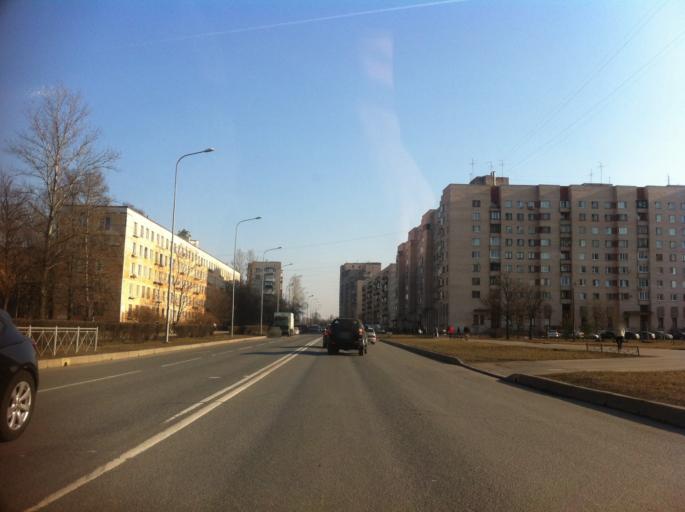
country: RU
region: St.-Petersburg
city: Dachnoye
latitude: 59.8443
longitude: 30.2327
